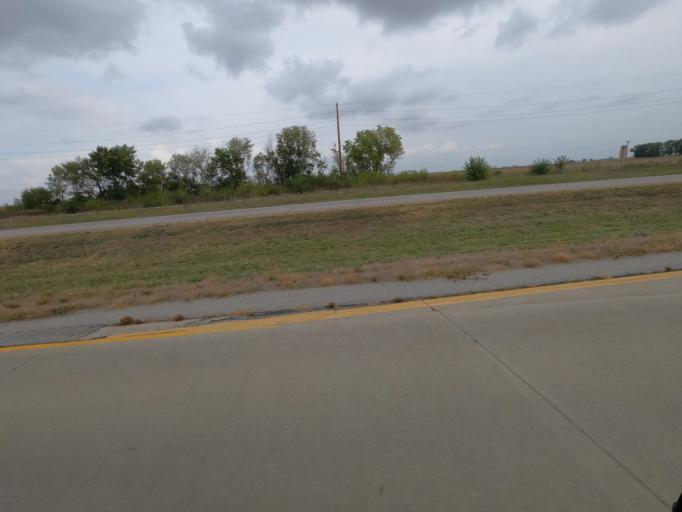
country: US
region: Iowa
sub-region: Jasper County
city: Monroe
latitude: 41.5667
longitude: -93.1604
